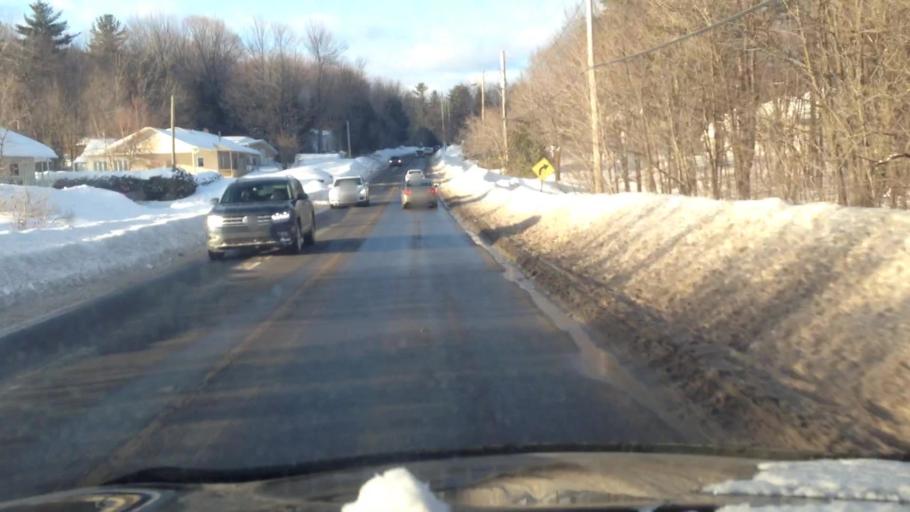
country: CA
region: Quebec
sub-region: Laurentides
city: Saint-Jerome
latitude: 45.8035
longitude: -73.9854
